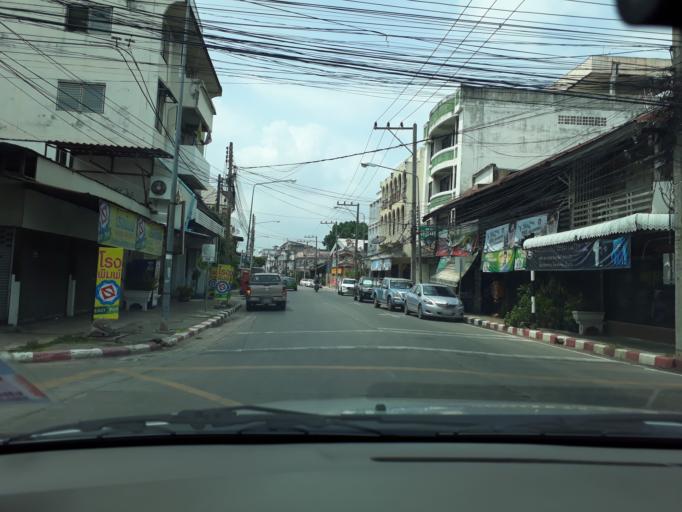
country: TH
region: Khon Kaen
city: Khon Kaen
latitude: 16.4277
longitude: 102.8373
